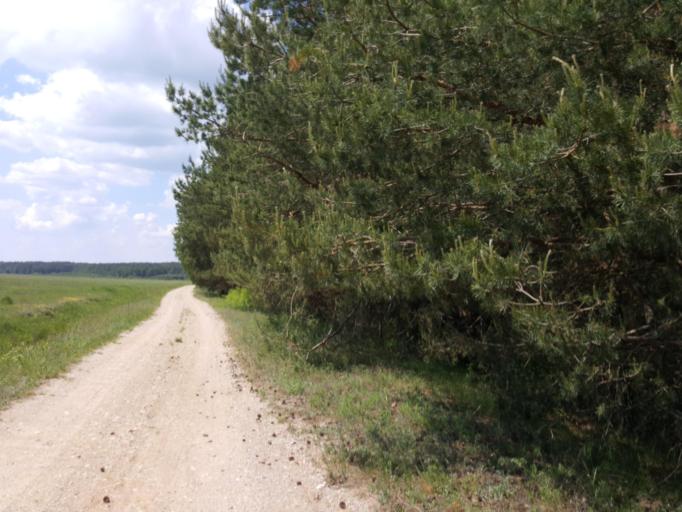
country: BY
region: Brest
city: Kamyanyuki
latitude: 52.5407
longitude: 23.7070
